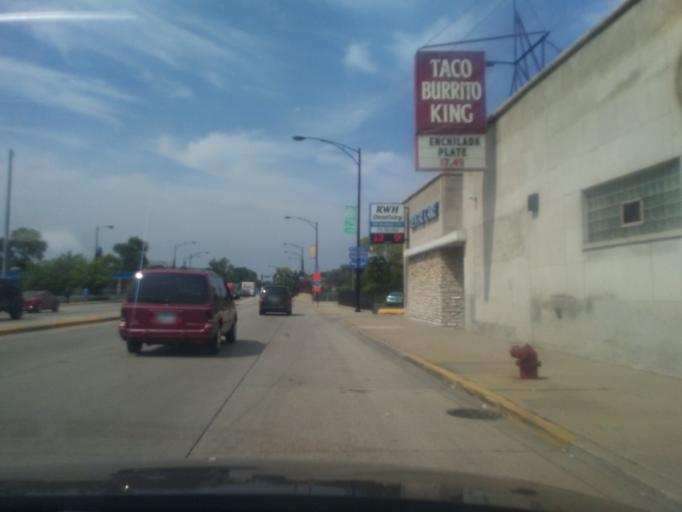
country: US
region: Illinois
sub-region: Cook County
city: Harwood Heights
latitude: 41.9813
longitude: -87.8068
